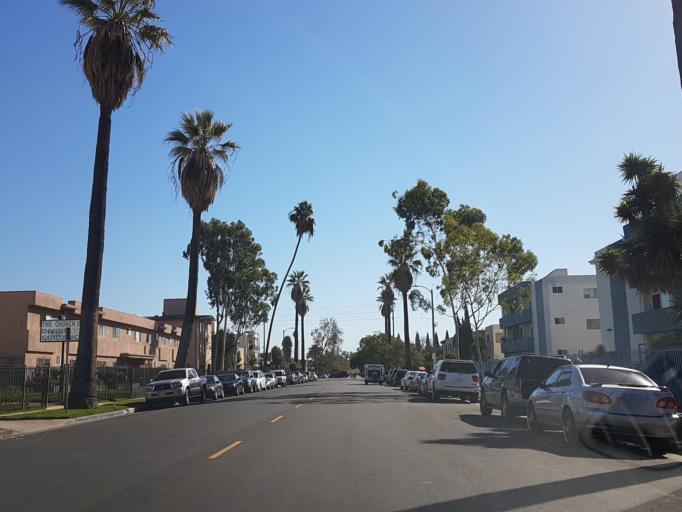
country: US
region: California
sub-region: Los Angeles County
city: Hollywood
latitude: 34.0451
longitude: -118.3131
